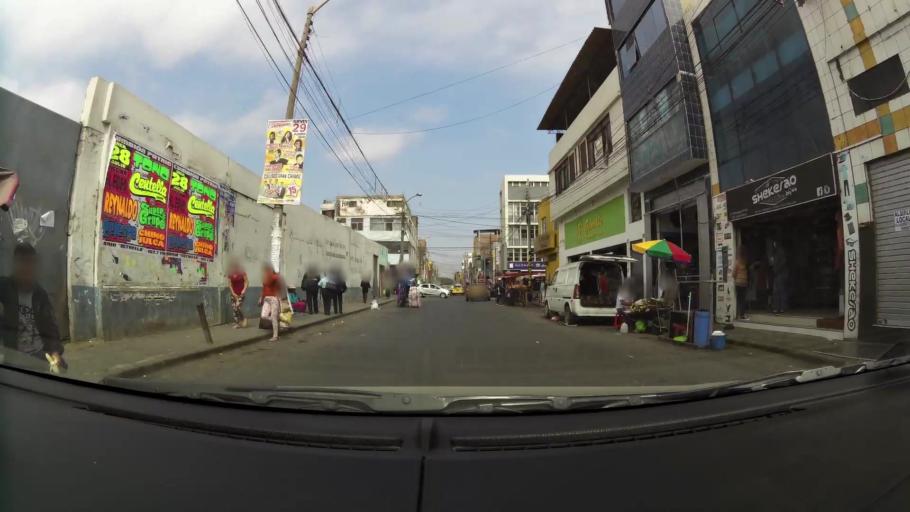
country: PE
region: La Libertad
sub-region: Provincia de Trujillo
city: Trujillo
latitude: -8.1137
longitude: -79.0235
